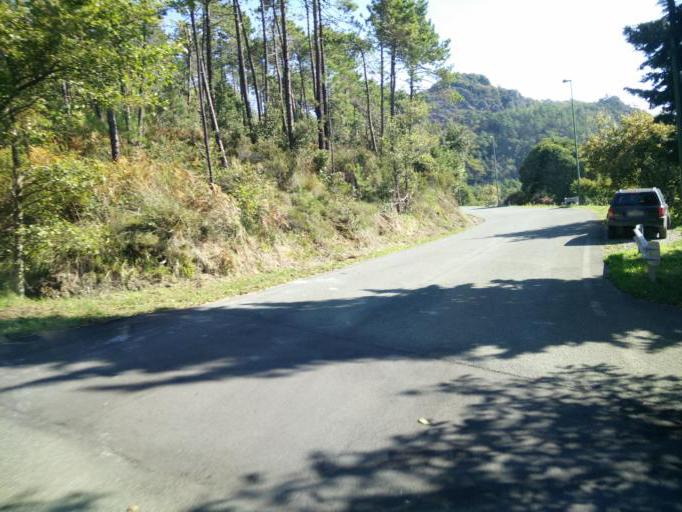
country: IT
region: Liguria
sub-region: Provincia di La Spezia
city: Framura
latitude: 44.2336
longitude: 9.5771
